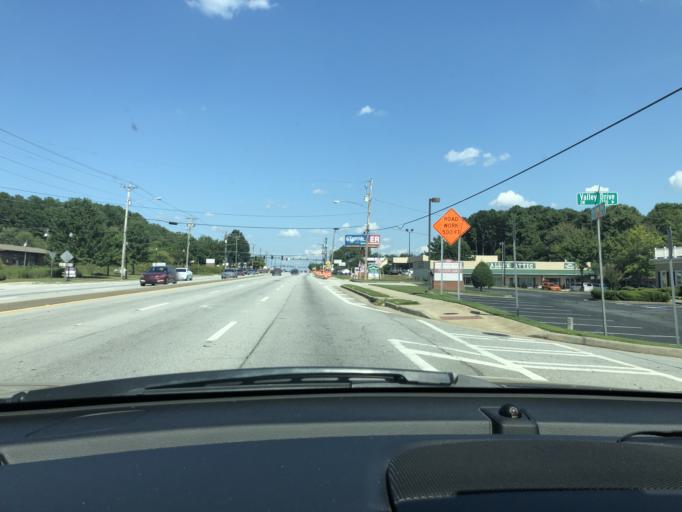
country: US
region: Georgia
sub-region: Gwinnett County
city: Snellville
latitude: 33.8544
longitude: -84.0308
